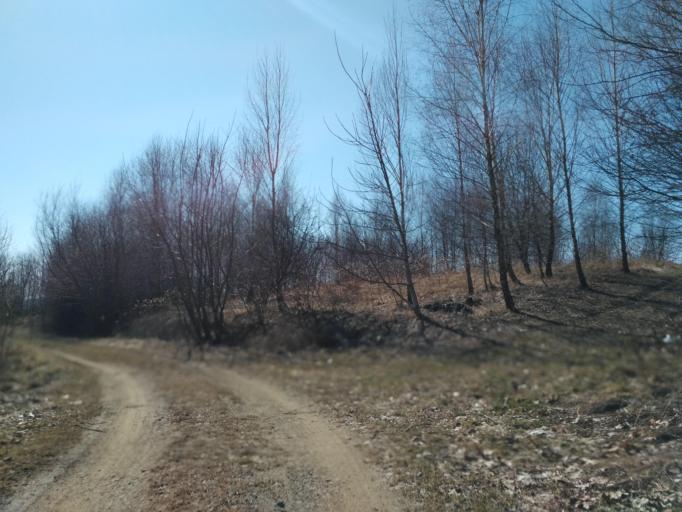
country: PL
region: Subcarpathian Voivodeship
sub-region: Powiat brzozowski
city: Domaradz
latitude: 49.8039
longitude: 21.9588
